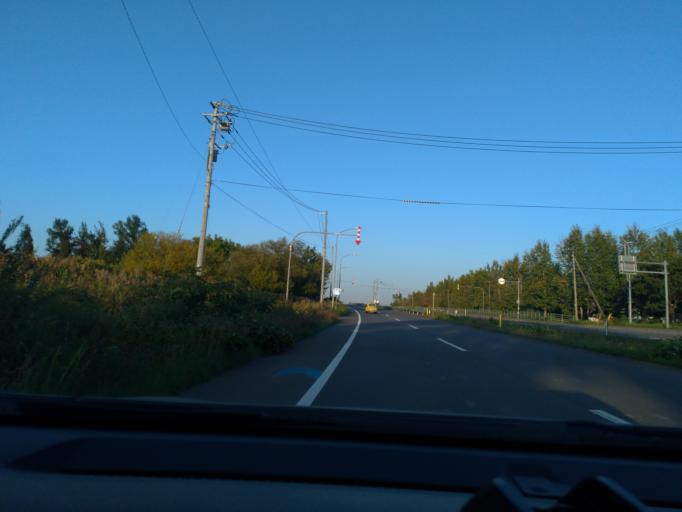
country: JP
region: Hokkaido
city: Ishikari
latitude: 43.1690
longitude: 141.4108
